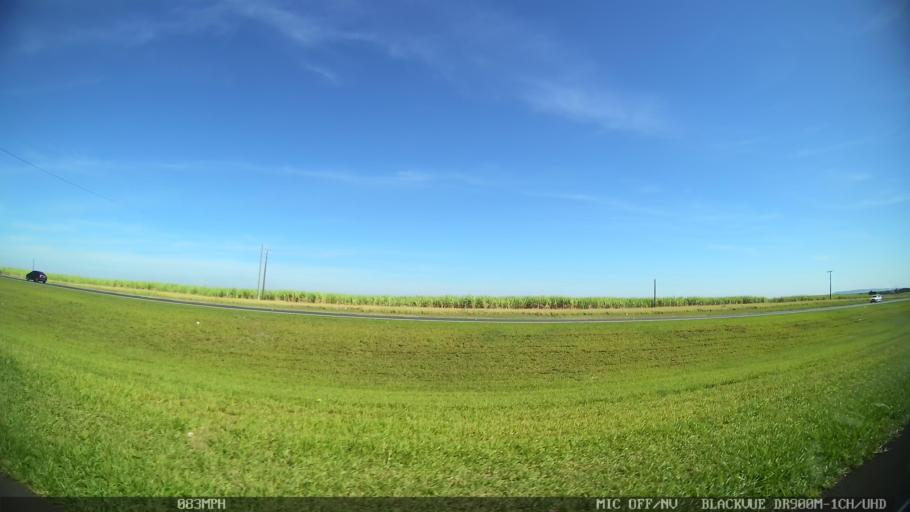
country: BR
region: Sao Paulo
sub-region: Santa Rita Do Passa Quatro
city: Santa Rita do Passa Quatro
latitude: -21.6943
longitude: -47.5982
